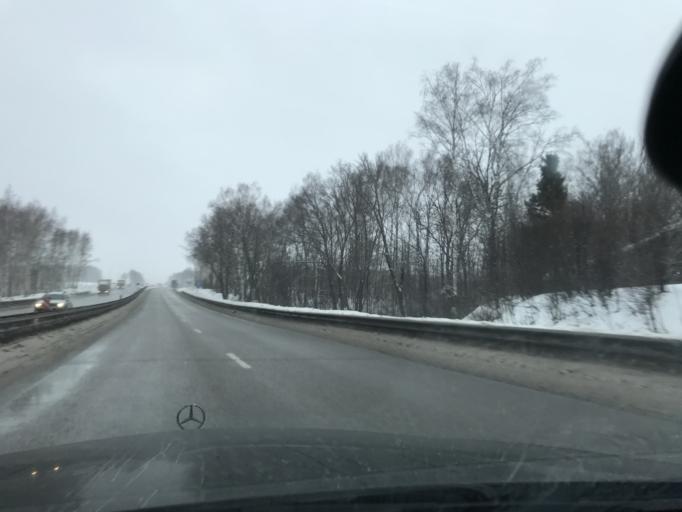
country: RU
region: Vladimir
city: Novovyazniki
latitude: 56.1915
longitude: 42.3856
